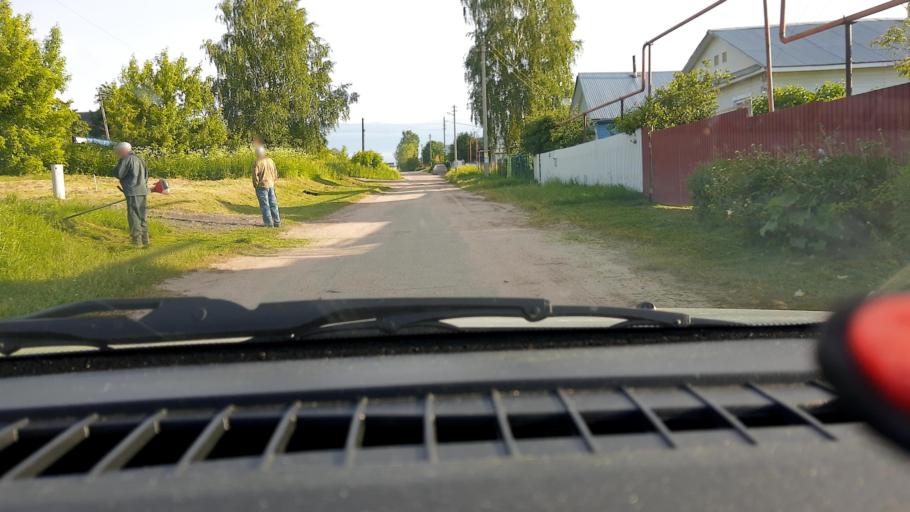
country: RU
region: Nizjnij Novgorod
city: Afonino
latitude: 56.1253
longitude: 44.0266
